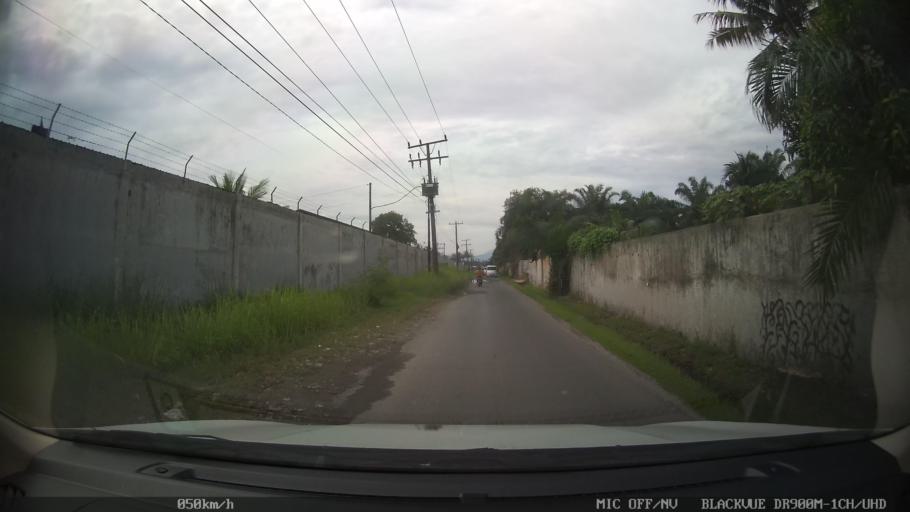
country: ID
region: North Sumatra
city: Sunggal
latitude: 3.5856
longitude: 98.5775
